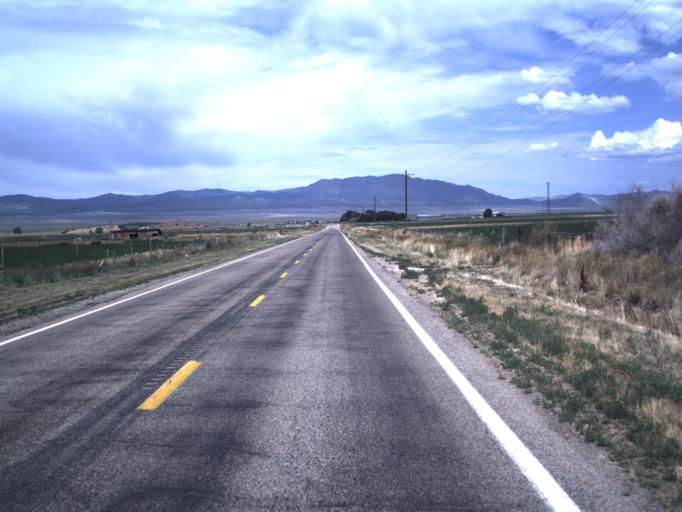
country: US
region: Utah
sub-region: Iron County
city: Parowan
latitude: 37.9002
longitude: -112.7749
